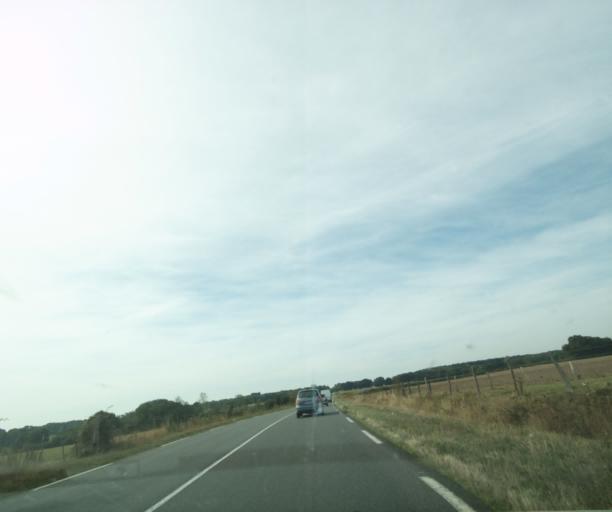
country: FR
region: Auvergne
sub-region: Departement de l'Allier
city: Lapalisse
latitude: 46.2353
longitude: 3.6014
